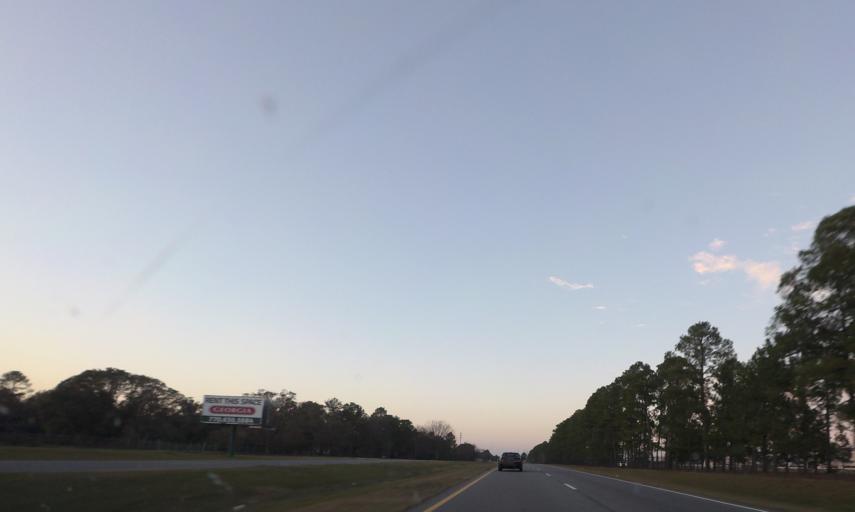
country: US
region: Georgia
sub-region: Houston County
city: Warner Robins
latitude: 32.6410
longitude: -83.6065
